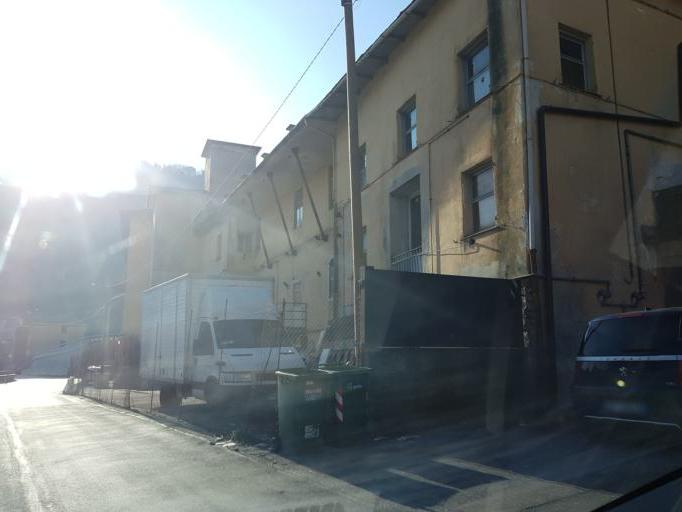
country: IT
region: Liguria
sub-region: Provincia di Genova
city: Campomorone
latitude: 44.5072
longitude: 8.8873
